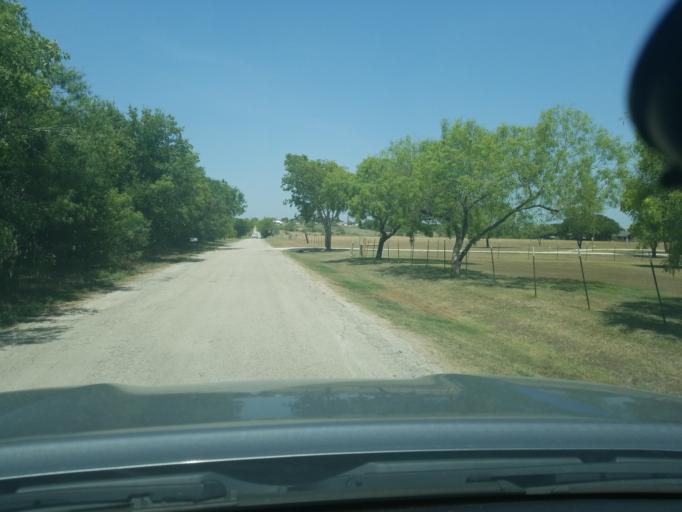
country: US
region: Texas
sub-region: Guadalupe County
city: Marion
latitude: 29.5739
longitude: -98.1834
